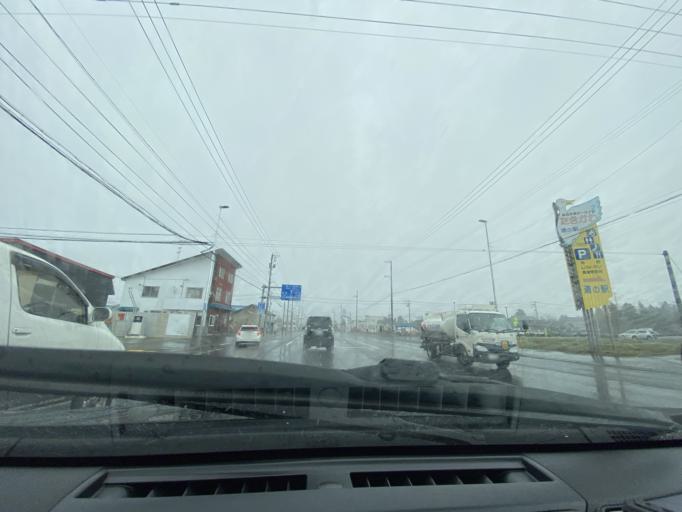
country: JP
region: Hokkaido
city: Takikawa
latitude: 43.6235
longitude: 141.9402
